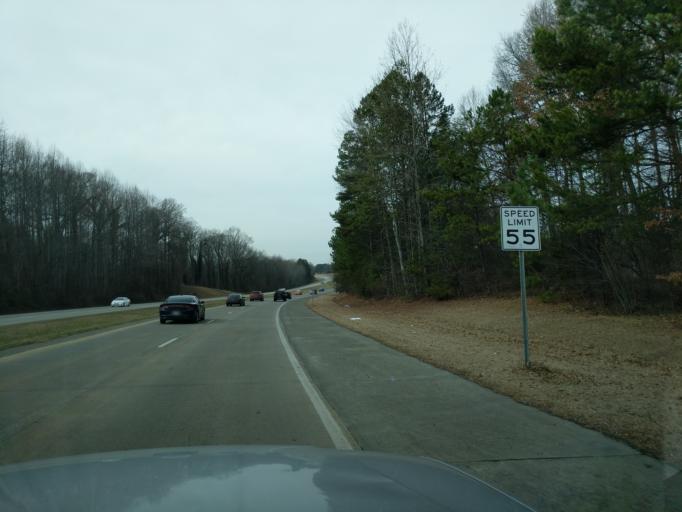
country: US
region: North Carolina
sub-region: Mecklenburg County
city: Charlotte
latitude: 35.1818
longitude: -80.8925
